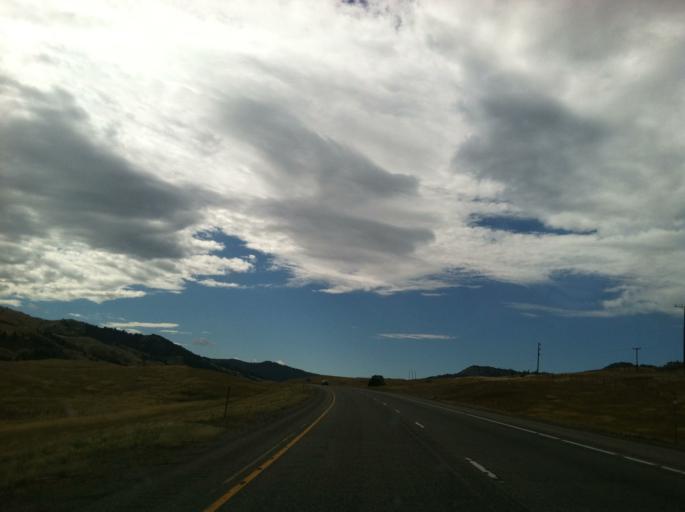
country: US
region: Montana
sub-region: Park County
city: Livingston
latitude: 45.6642
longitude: -110.6972
